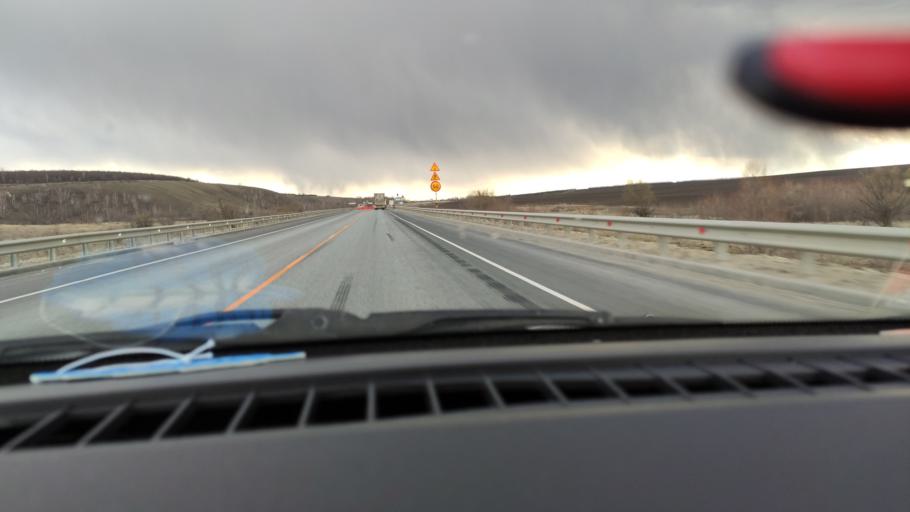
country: RU
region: Saratov
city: Yelshanka
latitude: 51.8649
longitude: 46.5014
